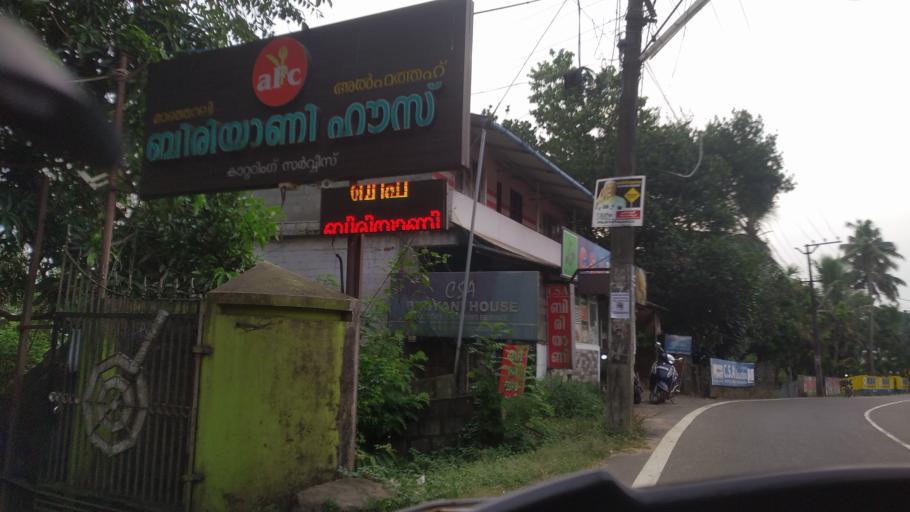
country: IN
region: Kerala
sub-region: Ernakulam
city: Elur
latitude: 10.1507
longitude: 76.2656
